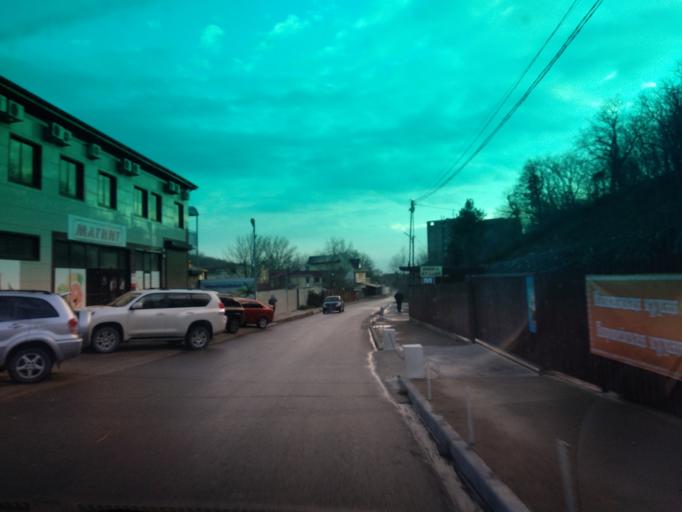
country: RU
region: Krasnodarskiy
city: Novomikhaylovskiy
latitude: 44.2619
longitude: 38.8227
